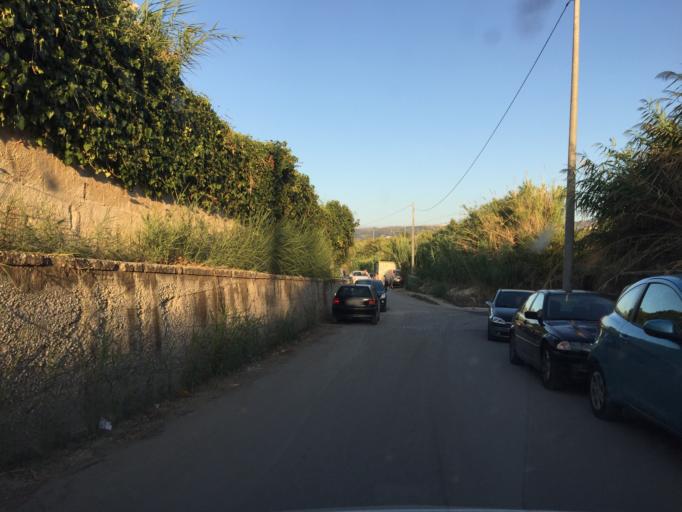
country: IT
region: Calabria
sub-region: Provincia di Vibo-Valentia
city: Briatico
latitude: 38.7209
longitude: 16.0561
